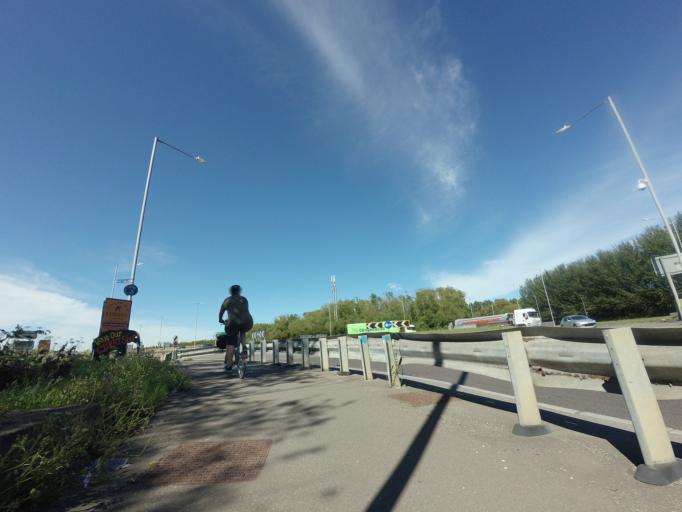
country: GB
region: England
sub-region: Kent
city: Sandwich
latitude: 51.3116
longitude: 1.3502
